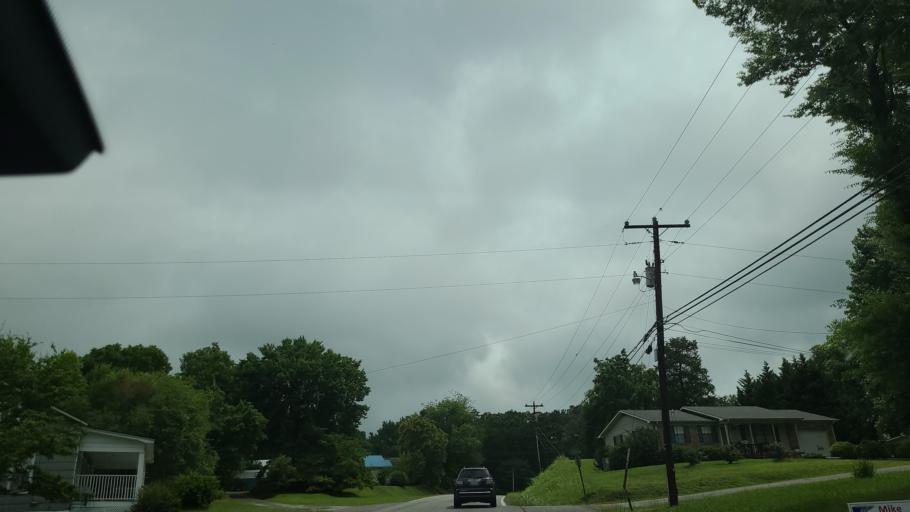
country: US
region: Tennessee
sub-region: Rhea County
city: Dayton
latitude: 35.4941
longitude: -85.0051
